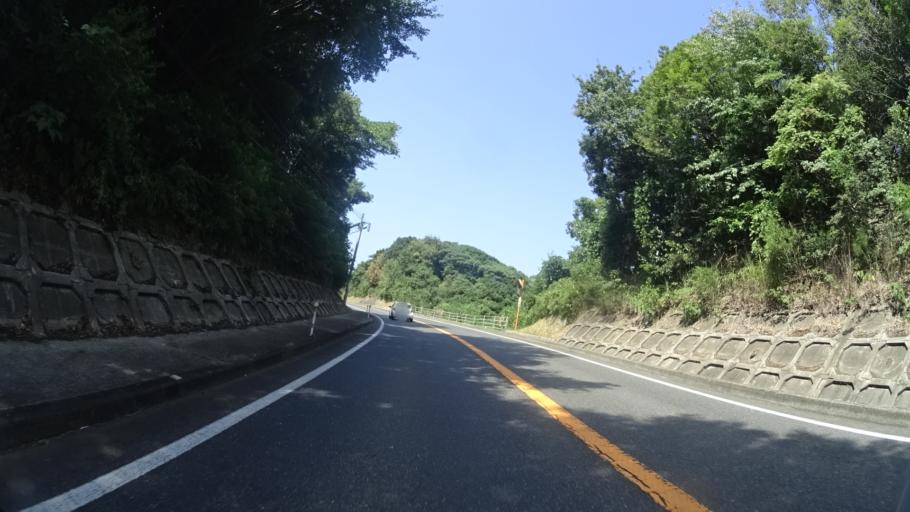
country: JP
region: Shimane
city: Masuda
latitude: 34.6726
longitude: 131.7281
